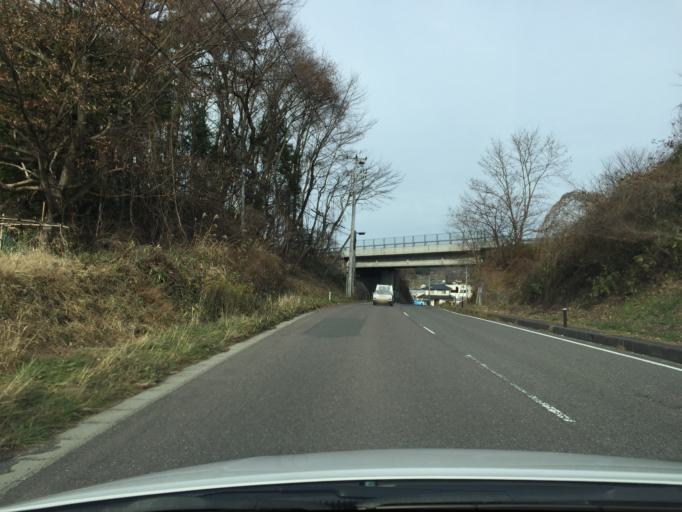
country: JP
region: Fukushima
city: Funehikimachi-funehiki
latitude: 37.3901
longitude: 140.5914
